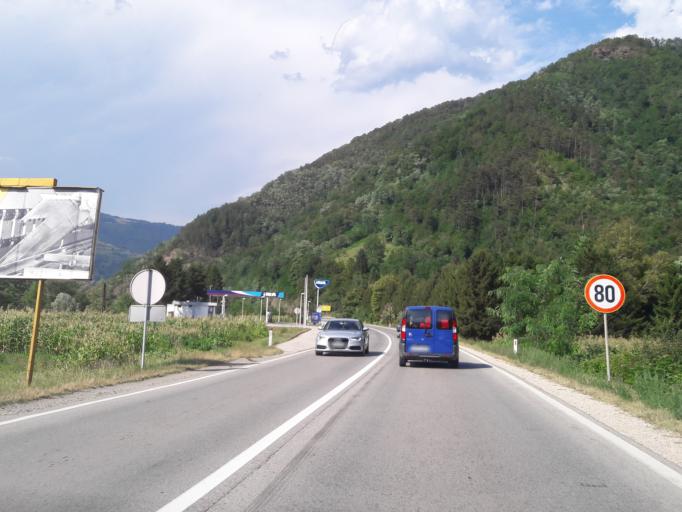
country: BA
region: Federation of Bosnia and Herzegovina
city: Zeljezno Polje
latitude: 44.3332
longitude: 17.9205
